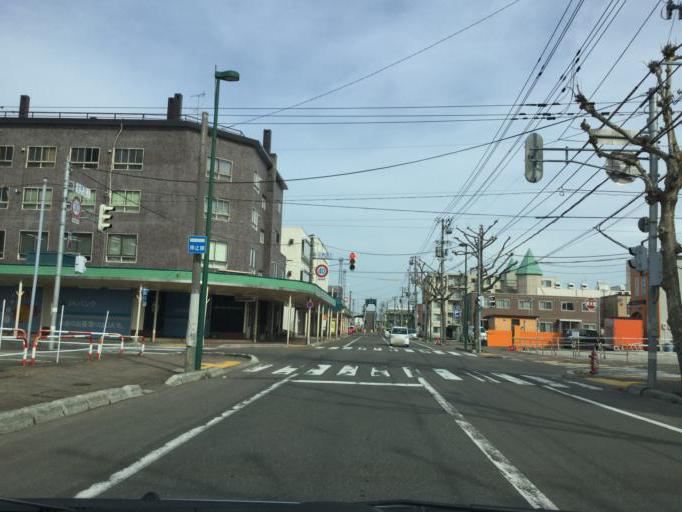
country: JP
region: Hokkaido
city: Iwamizawa
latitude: 43.2046
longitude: 141.7657
